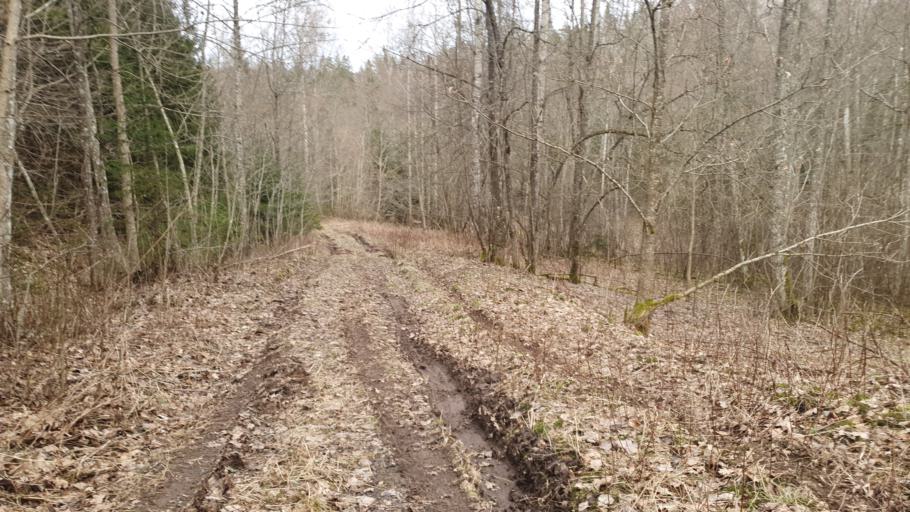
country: LV
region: Ligatne
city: Ligatne
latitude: 57.2413
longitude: 24.9702
